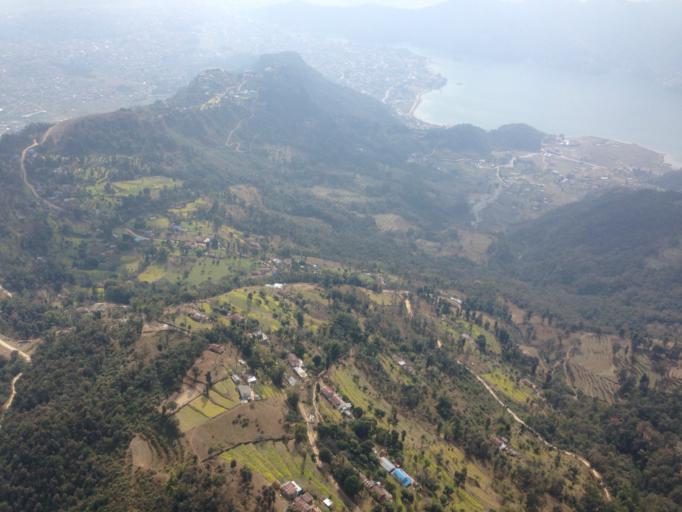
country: NP
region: Western Region
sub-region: Gandaki Zone
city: Pokhara
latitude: 28.2445
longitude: 83.9613
